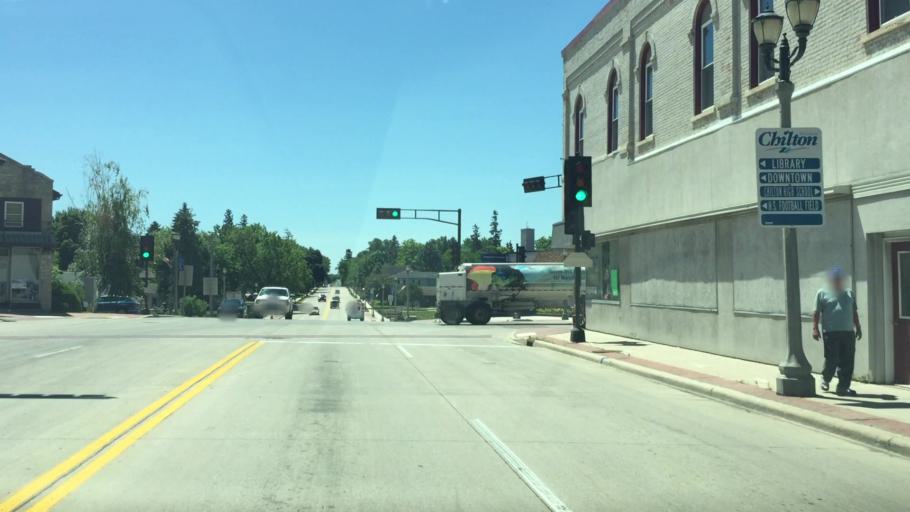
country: US
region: Wisconsin
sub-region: Calumet County
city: Chilton
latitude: 44.0291
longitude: -88.1629
